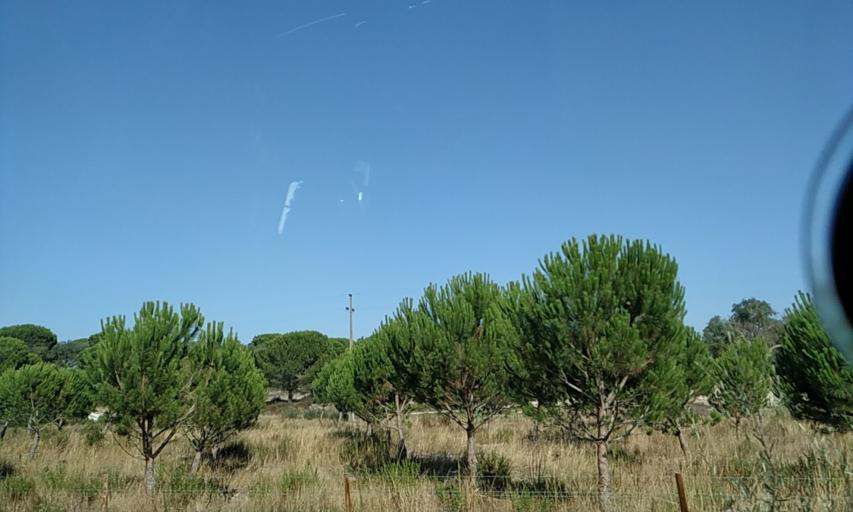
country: PT
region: Evora
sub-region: Vendas Novas
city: Vendas Novas
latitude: 38.7874
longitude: -8.5826
